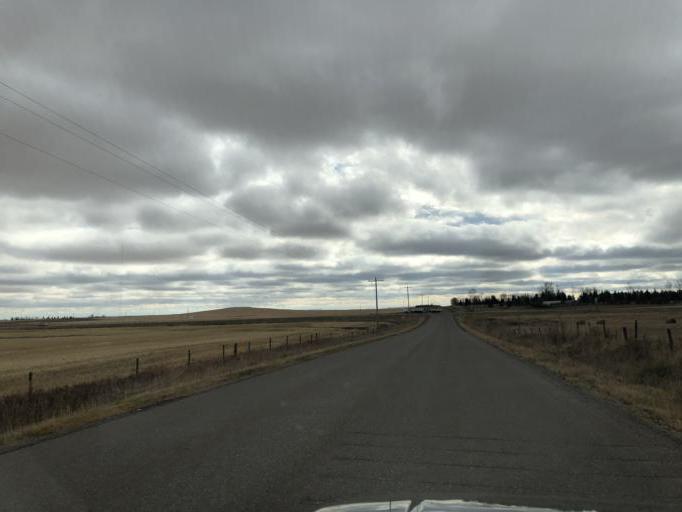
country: CA
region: Alberta
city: Chestermere
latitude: 50.9096
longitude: -113.8830
